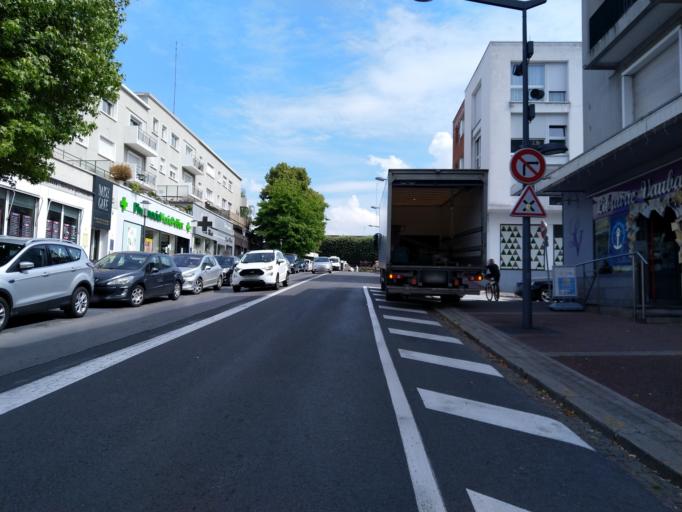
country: FR
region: Nord-Pas-de-Calais
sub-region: Departement du Nord
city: Maubeuge
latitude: 50.2776
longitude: 3.9740
